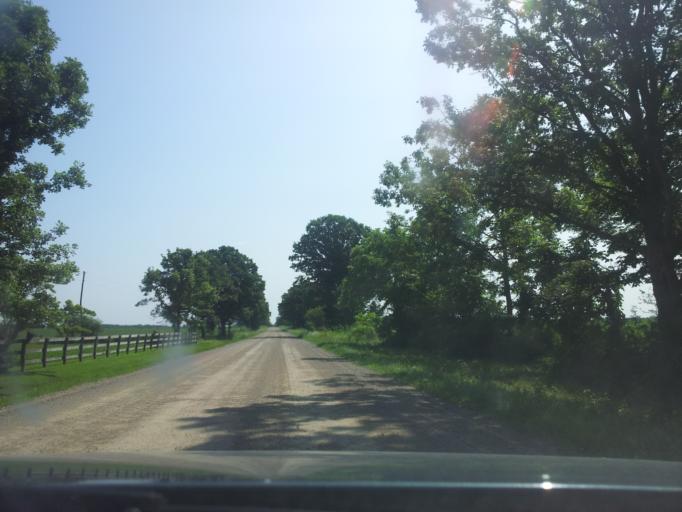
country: CA
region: Ontario
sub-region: Oxford County
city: Woodstock
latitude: 42.9542
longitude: -80.6188
